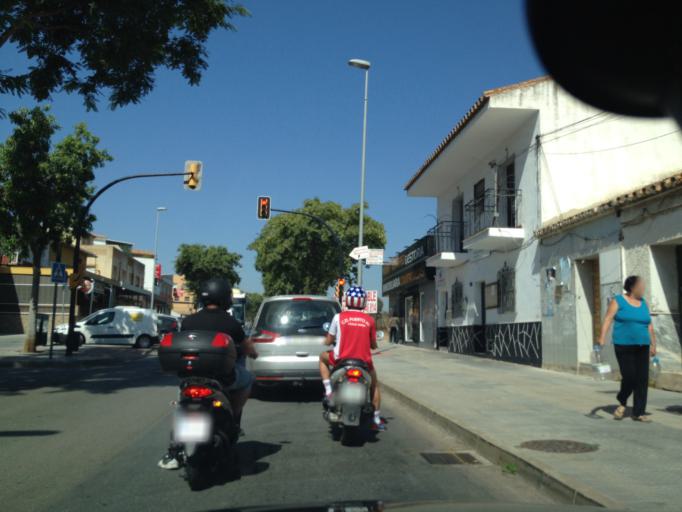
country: ES
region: Andalusia
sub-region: Provincia de Malaga
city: Alhaurin de la Torre
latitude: 36.7272
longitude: -4.5436
